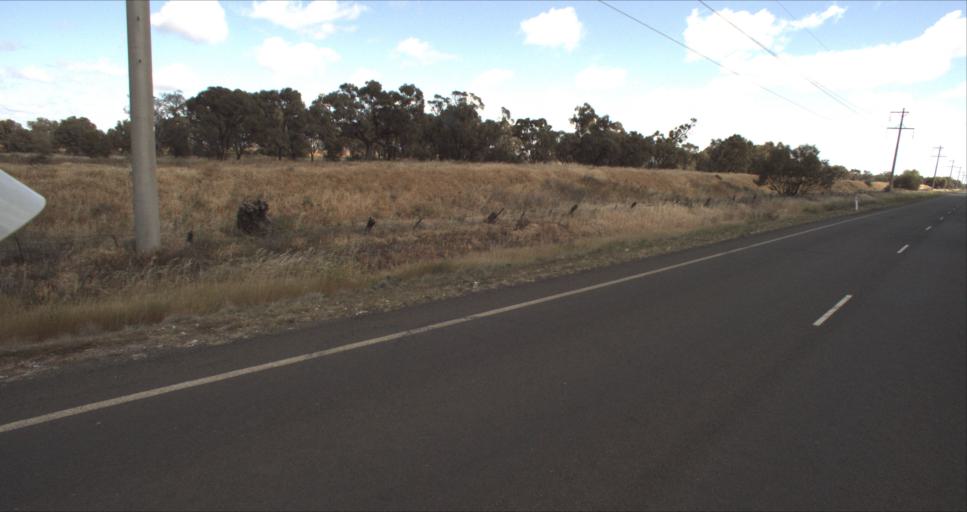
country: AU
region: New South Wales
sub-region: Murrumbidgee Shire
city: Darlington Point
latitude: -34.5318
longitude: 146.1738
